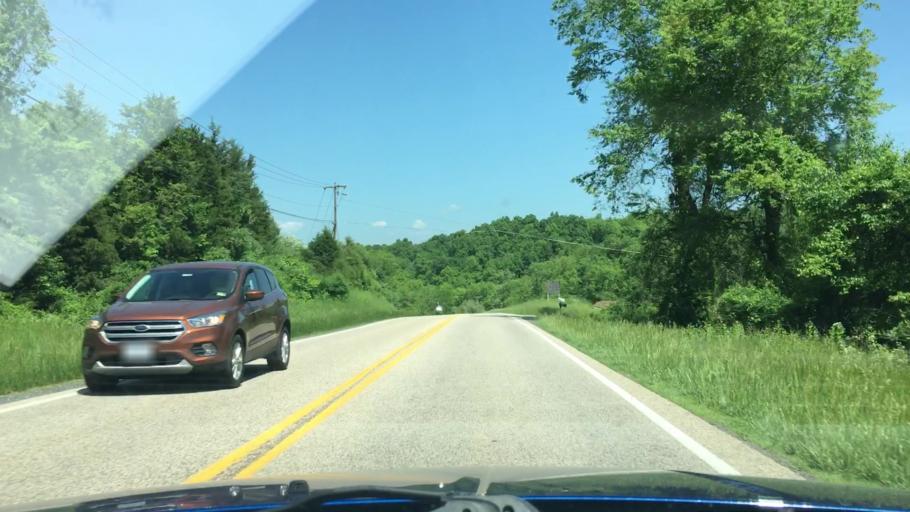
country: US
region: Virginia
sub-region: City of Staunton
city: Staunton
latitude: 38.1861
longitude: -79.1017
